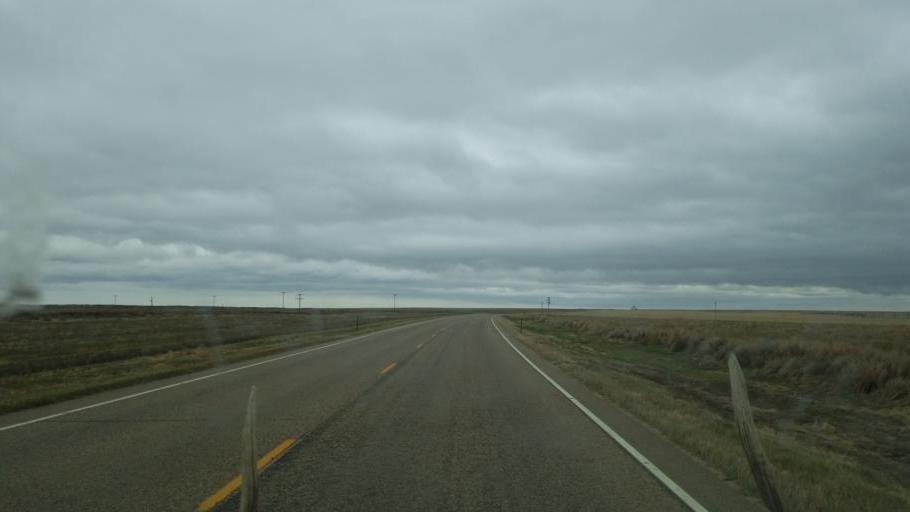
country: US
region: Colorado
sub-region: Cheyenne County
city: Cheyenne Wells
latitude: 38.8108
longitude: -102.5877
